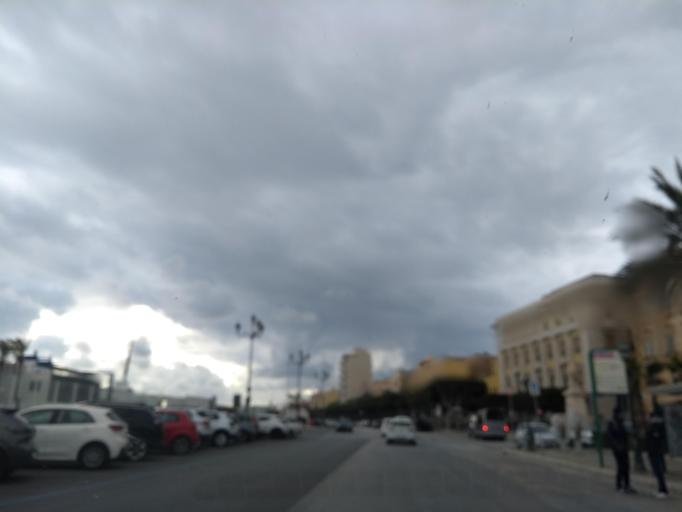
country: IT
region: Sicily
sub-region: Trapani
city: Trapani
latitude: 38.0141
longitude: 12.5085
